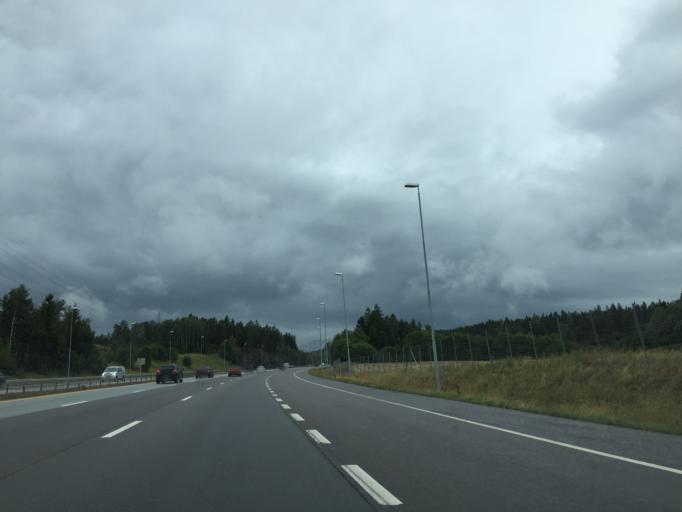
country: NO
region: Akershus
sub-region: Lorenskog
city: Kjenn
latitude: 59.9651
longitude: 10.9837
